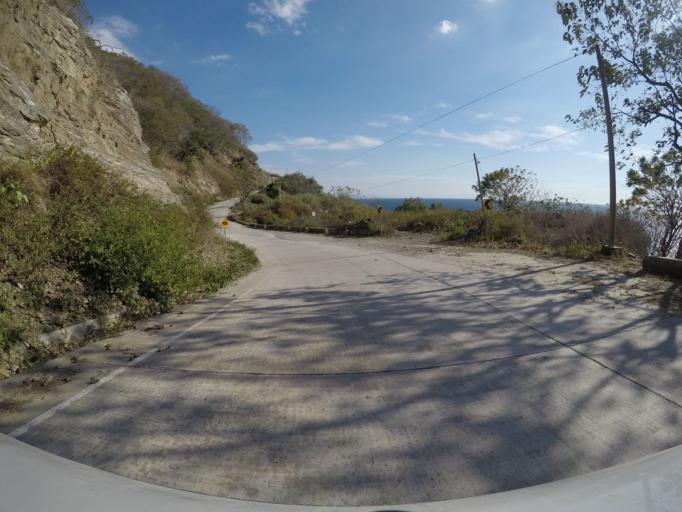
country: TL
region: Liquica
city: Maubara
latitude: -8.6682
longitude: 125.1092
